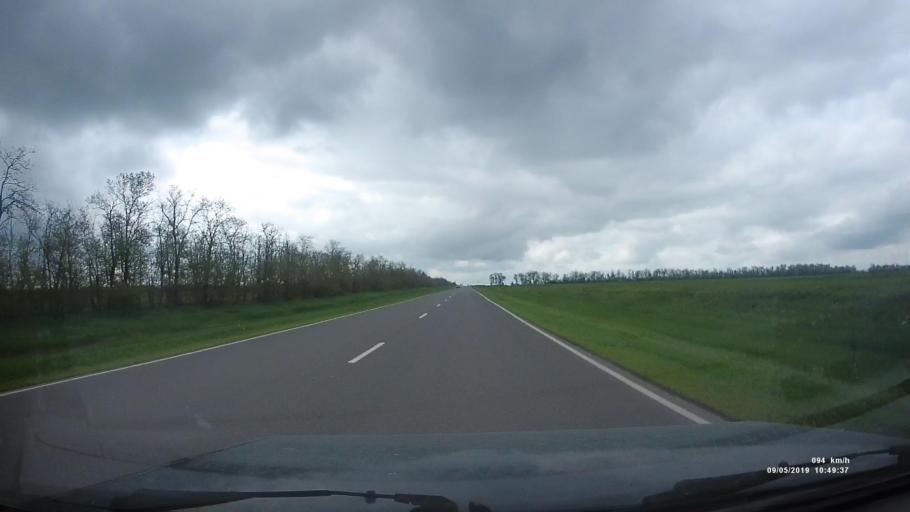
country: RU
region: Rostov
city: Peshkovo
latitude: 46.9403
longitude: 39.3560
